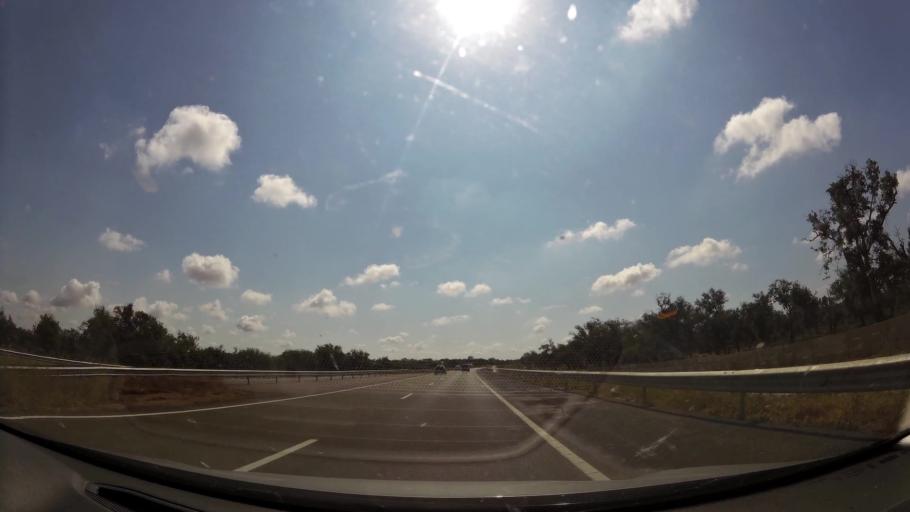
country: MA
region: Rabat-Sale-Zemmour-Zaer
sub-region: Skhirate-Temara
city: Temara
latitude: 33.8386
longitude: -6.8715
